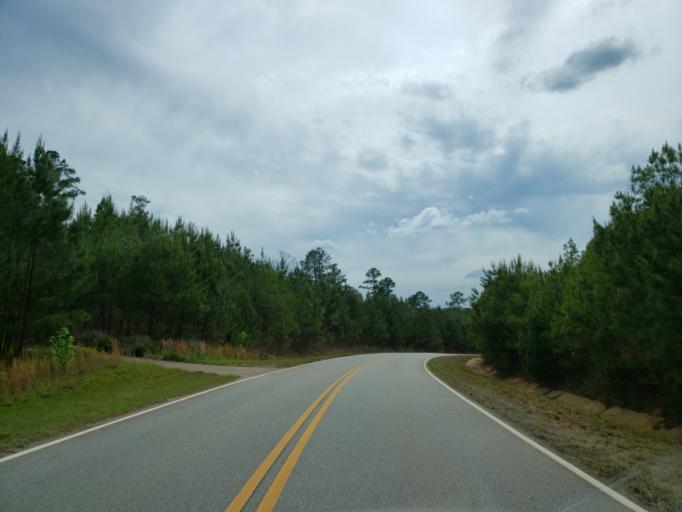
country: US
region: Georgia
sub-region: Monroe County
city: Forsyth
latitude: 32.9602
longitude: -83.9114
